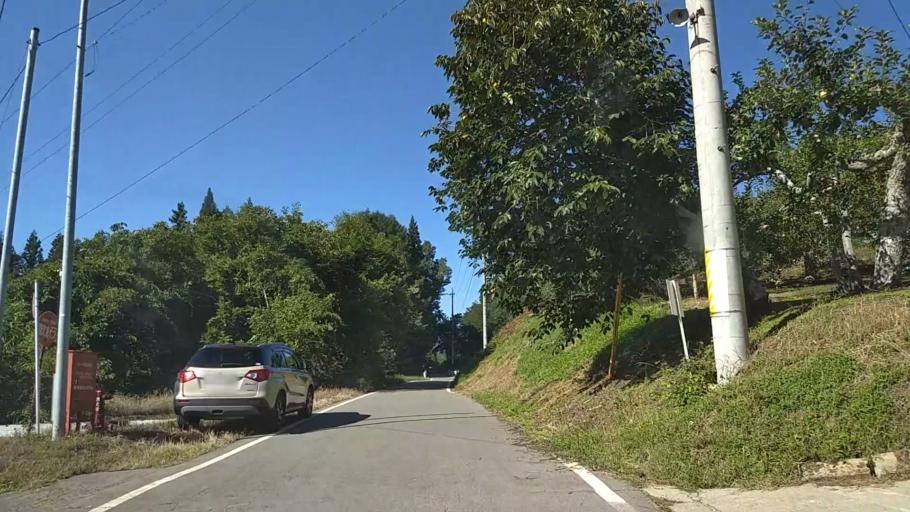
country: JP
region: Nagano
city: Nagano-shi
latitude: 36.5841
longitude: 138.0886
